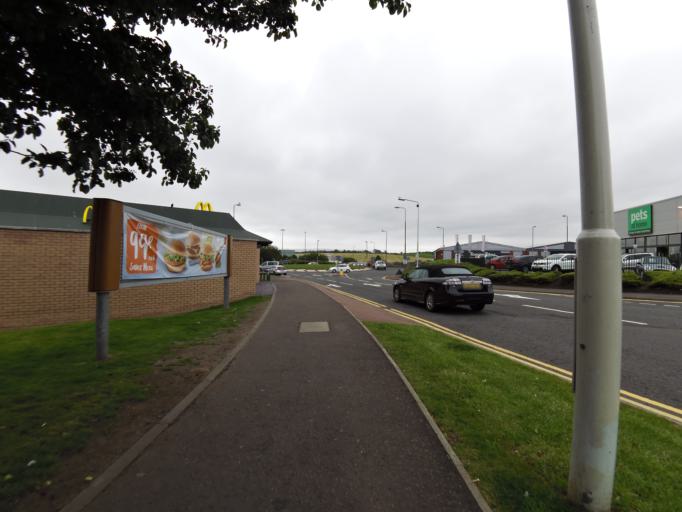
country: GB
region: Scotland
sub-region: East Lothian
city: Musselburgh
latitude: 55.9341
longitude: -3.1012
